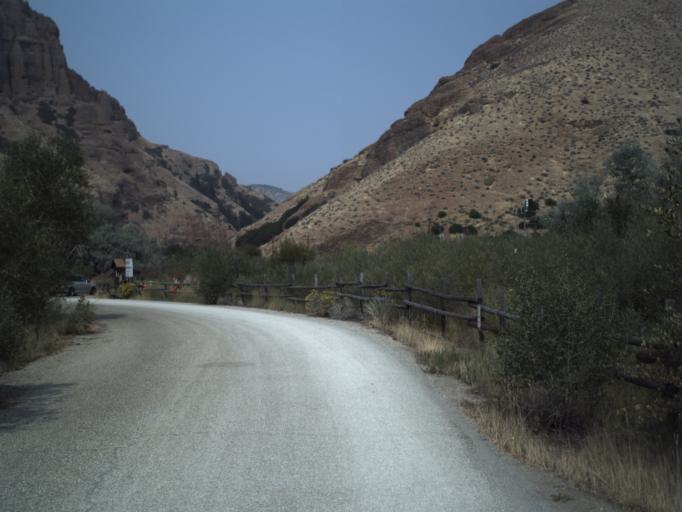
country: US
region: Utah
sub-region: Morgan County
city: Morgan
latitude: 41.0445
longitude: -111.5219
